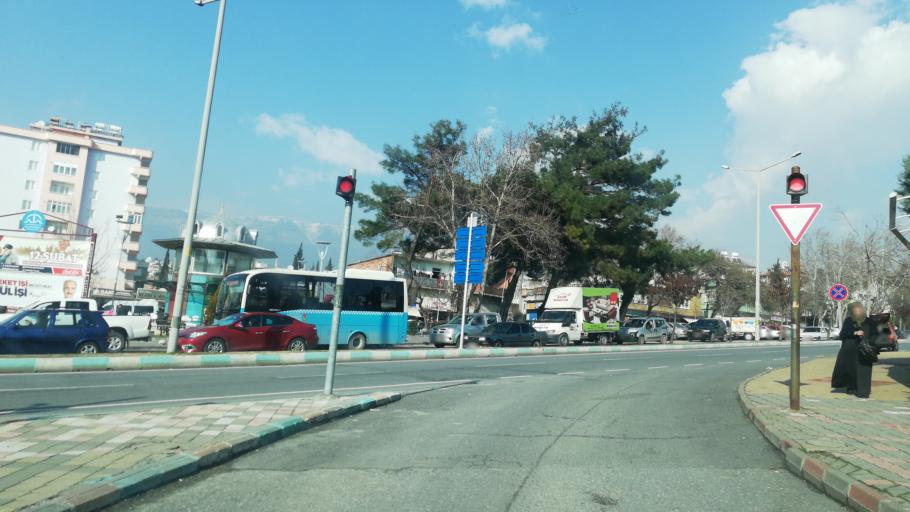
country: TR
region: Kahramanmaras
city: Kahramanmaras
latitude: 37.5778
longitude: 36.9334
